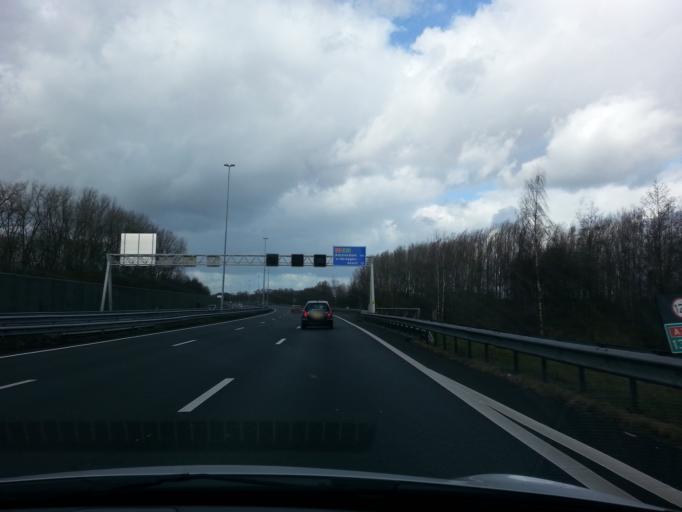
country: NL
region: North Brabant
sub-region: Gemeente Boxtel
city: Boxtel
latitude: 51.5854
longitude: 5.3546
